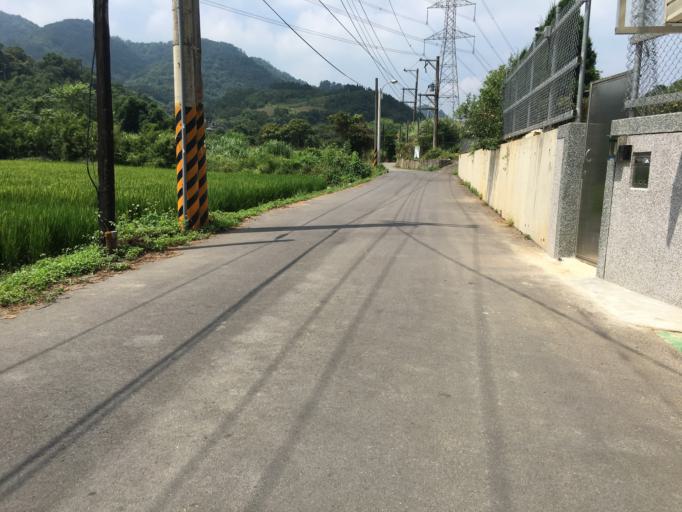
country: TW
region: Taiwan
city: Daxi
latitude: 24.8269
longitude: 121.2319
